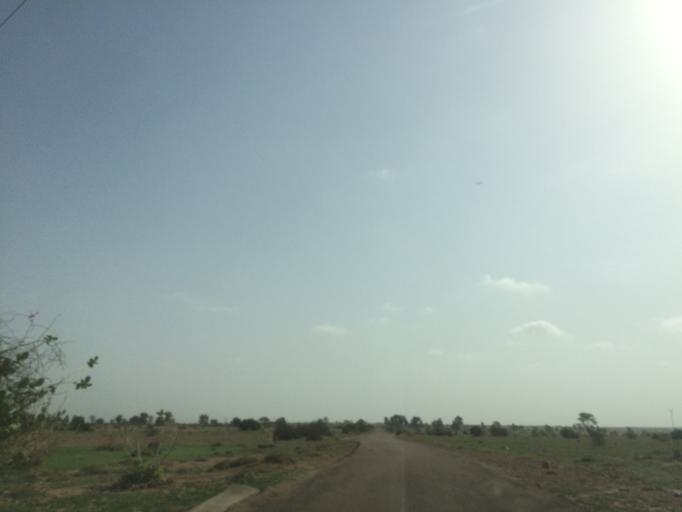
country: IN
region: Rajasthan
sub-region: Jaisalmer
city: Jaisalmer
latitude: 26.8073
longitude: 70.6960
